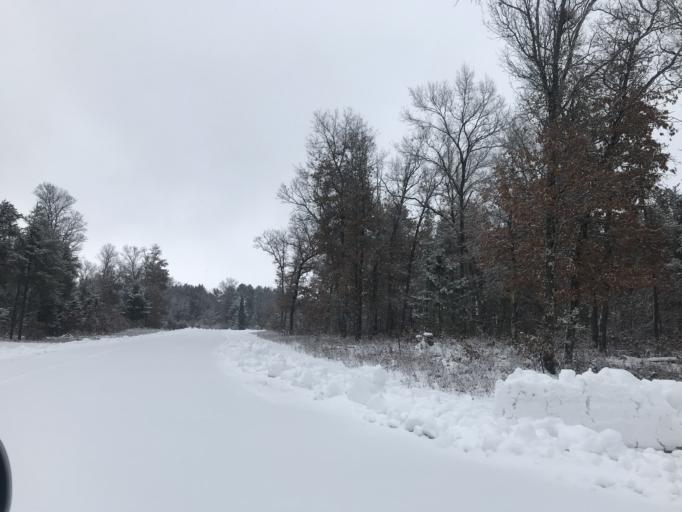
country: US
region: Wisconsin
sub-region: Oconto County
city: Gillett
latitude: 45.2930
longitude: -88.2196
